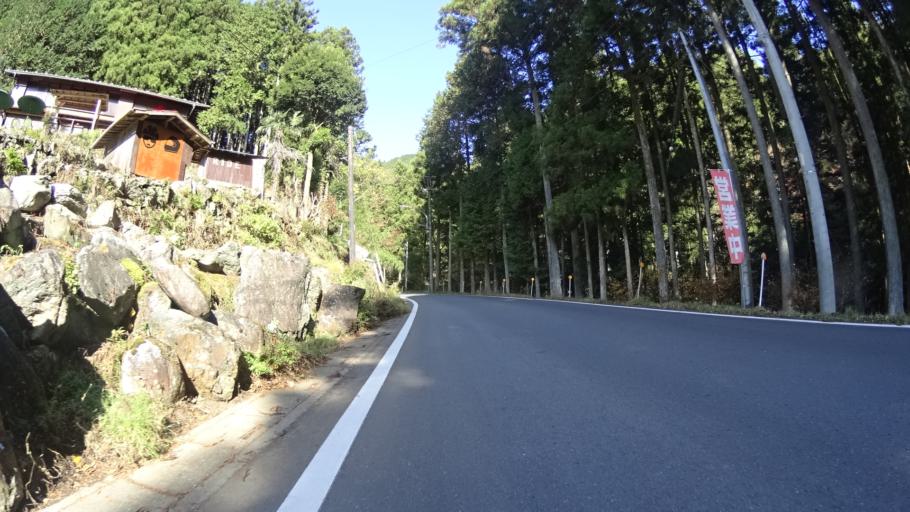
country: JP
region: Saitama
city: Chichibu
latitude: 35.9231
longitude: 139.1518
